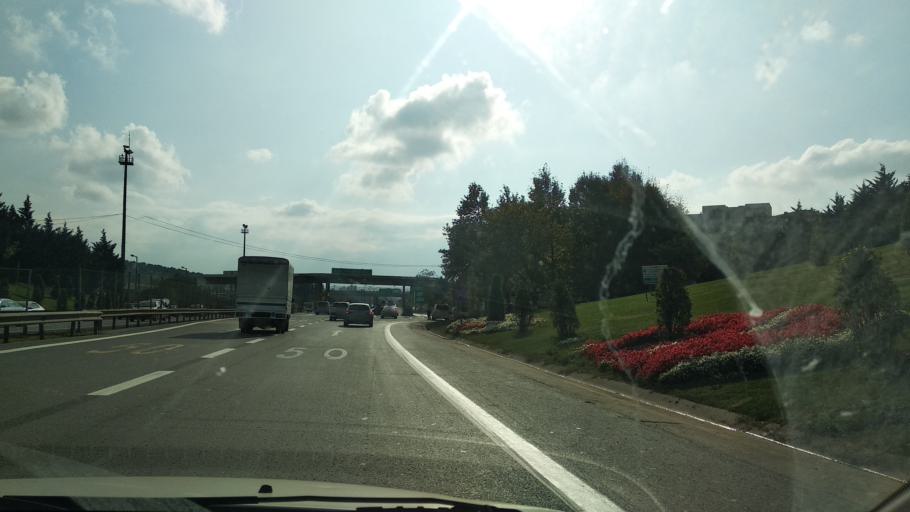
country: TR
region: Istanbul
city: Sultanbeyli
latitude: 40.9338
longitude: 29.3307
